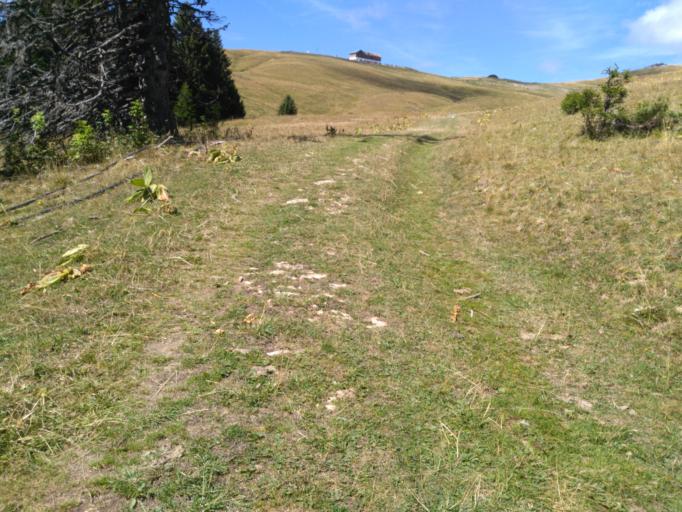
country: FR
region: Rhone-Alpes
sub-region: Departement de la Haute-Savoie
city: Viuz-la-Chiesaz
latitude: 45.7894
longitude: 6.1058
